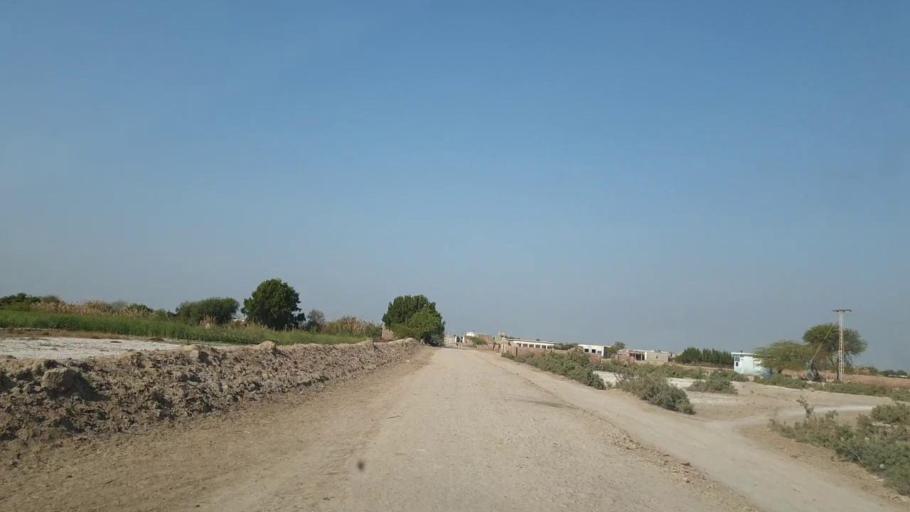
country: PK
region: Sindh
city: Tando Mittha Khan
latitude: 25.7503
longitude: 69.1968
